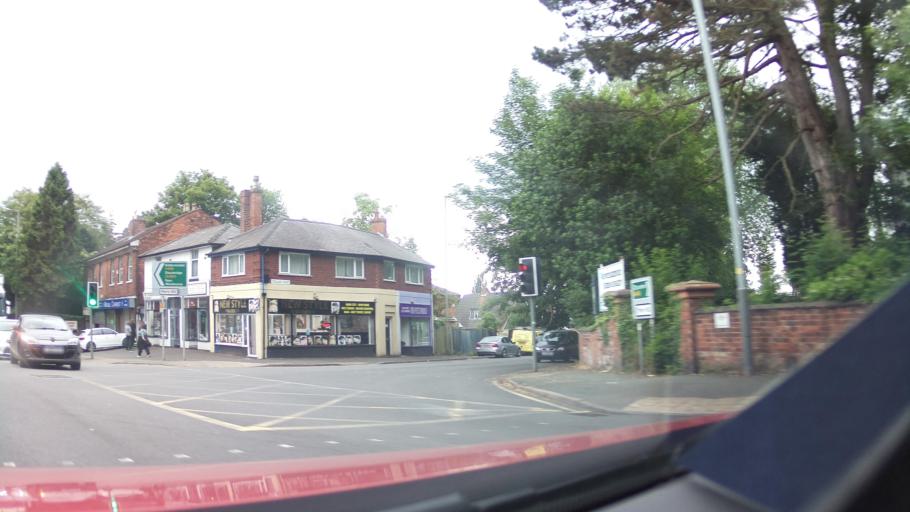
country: GB
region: England
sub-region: Wolverhampton
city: Wolverhampton
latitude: 52.5689
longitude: -2.1434
